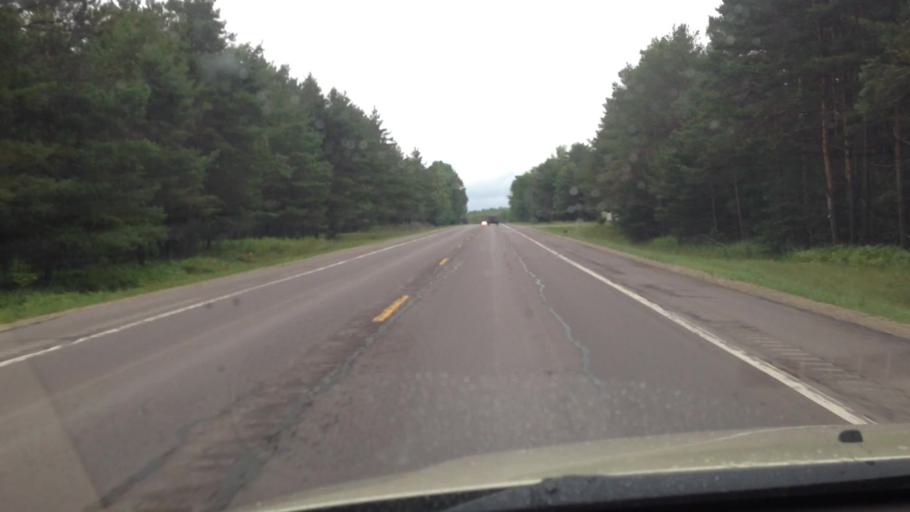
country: US
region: Michigan
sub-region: Schoolcraft County
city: Manistique
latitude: 46.0512
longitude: -85.9649
